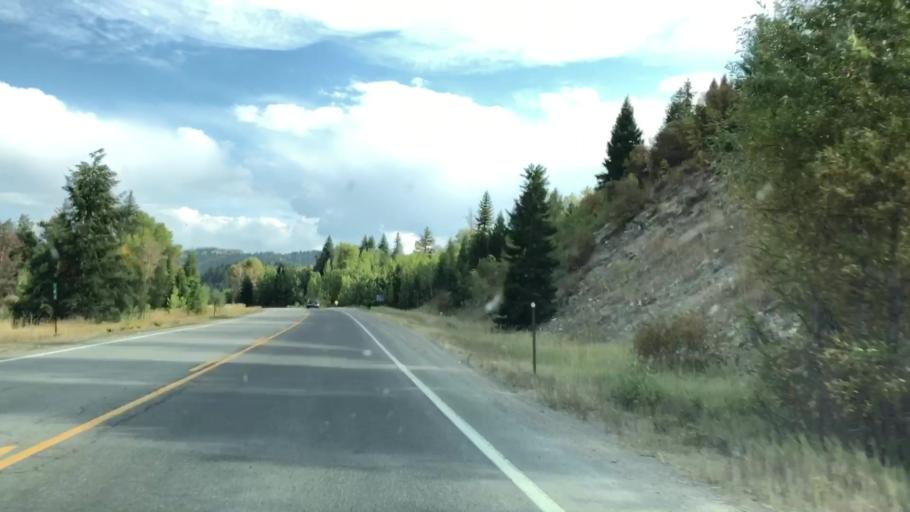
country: US
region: Wyoming
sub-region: Teton County
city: South Park
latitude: 43.3604
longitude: -110.7265
